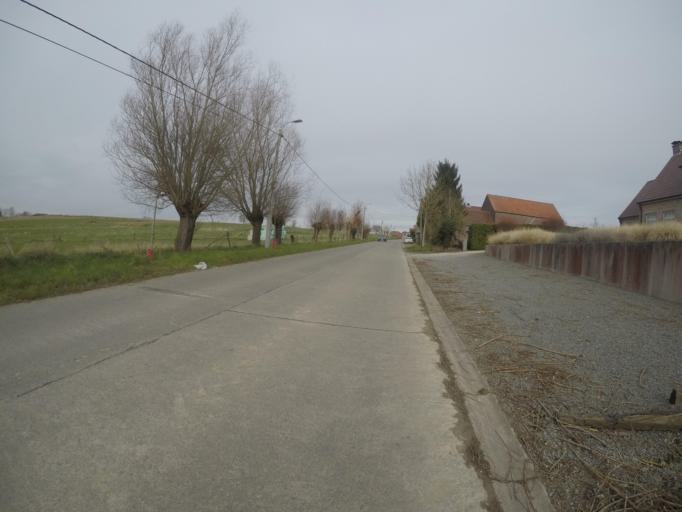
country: BE
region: Flanders
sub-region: Provincie Oost-Vlaanderen
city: Sint-Maria-Lierde
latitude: 50.7971
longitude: 3.8001
